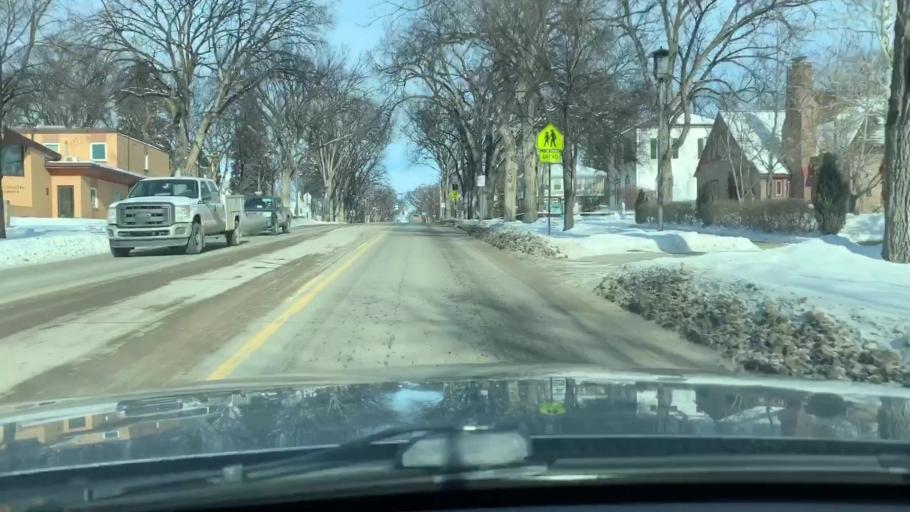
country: US
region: North Dakota
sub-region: Burleigh County
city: Bismarck
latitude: 46.8100
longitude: -100.7943
